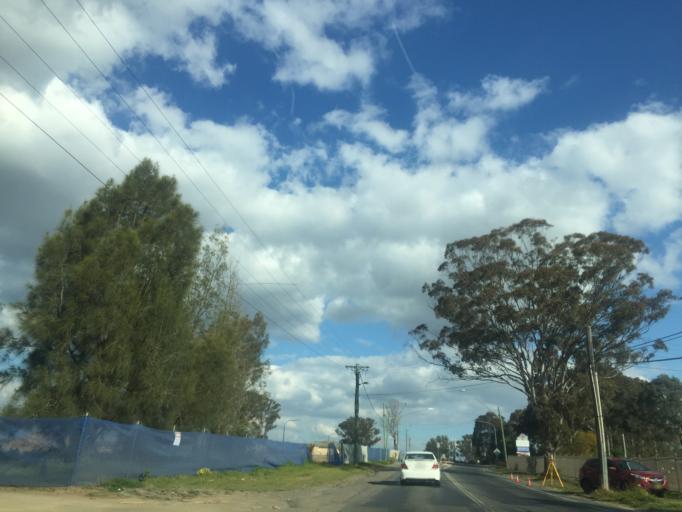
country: AU
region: New South Wales
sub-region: Blacktown
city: Quakers Hill
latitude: -33.7046
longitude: 150.8941
